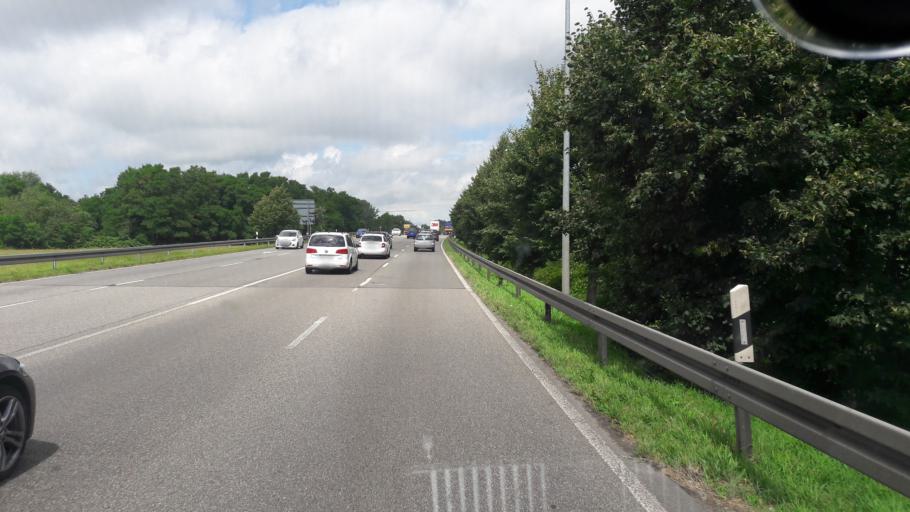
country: DE
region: Baden-Wuerttemberg
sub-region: Karlsruhe Region
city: Karlsruhe
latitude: 49.0399
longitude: 8.3628
